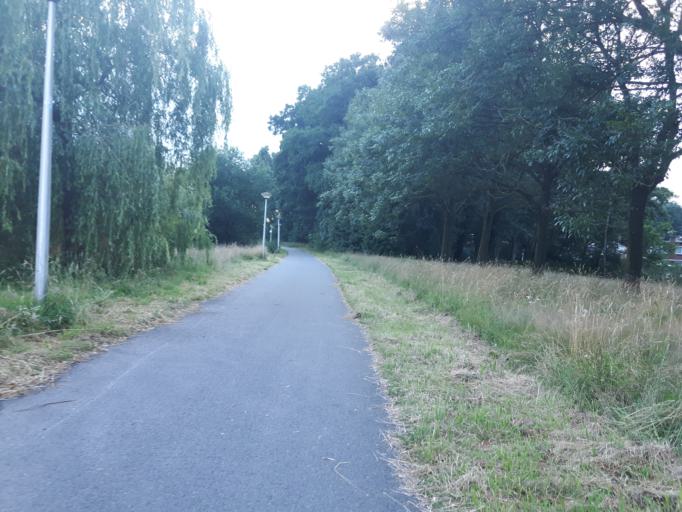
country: NL
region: Overijssel
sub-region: Gemeente Enschede
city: Enschede
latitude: 52.2028
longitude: 6.8732
